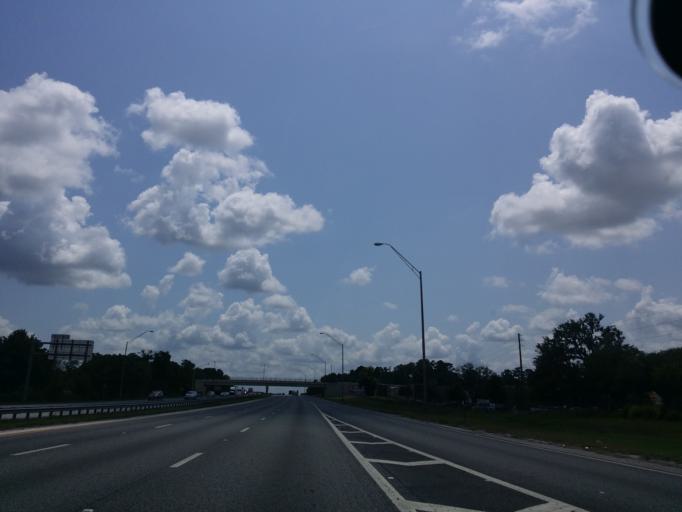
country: US
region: Florida
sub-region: Marion County
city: Ocala
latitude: 29.1464
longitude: -82.1853
